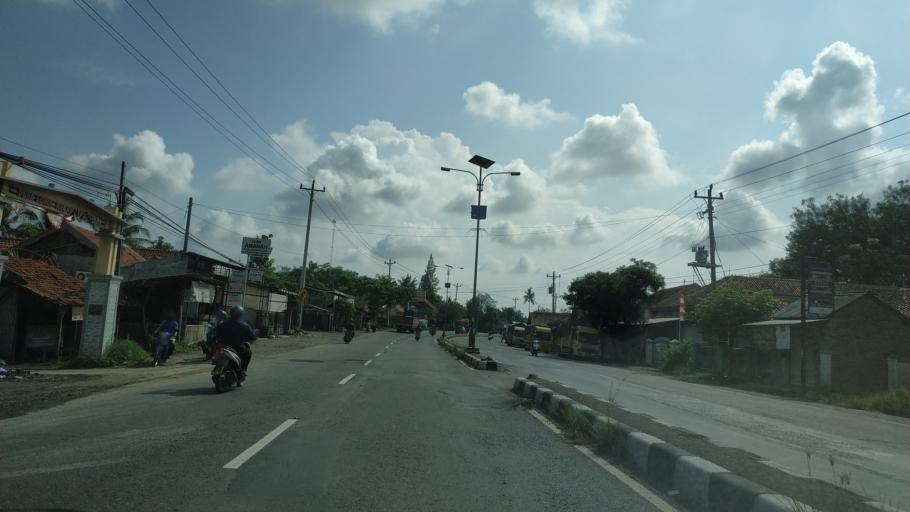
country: ID
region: Central Java
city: Comal
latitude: -6.8908
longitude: 109.5435
